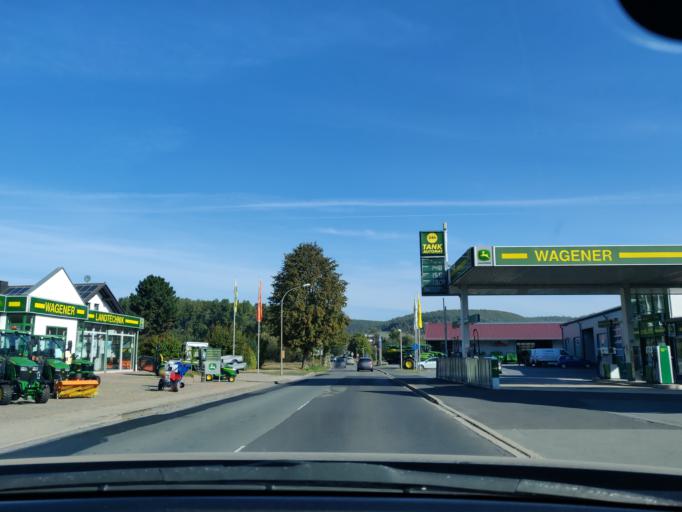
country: DE
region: Hesse
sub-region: Regierungsbezirk Kassel
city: Bad Wildungen
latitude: 51.1335
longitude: 9.1764
